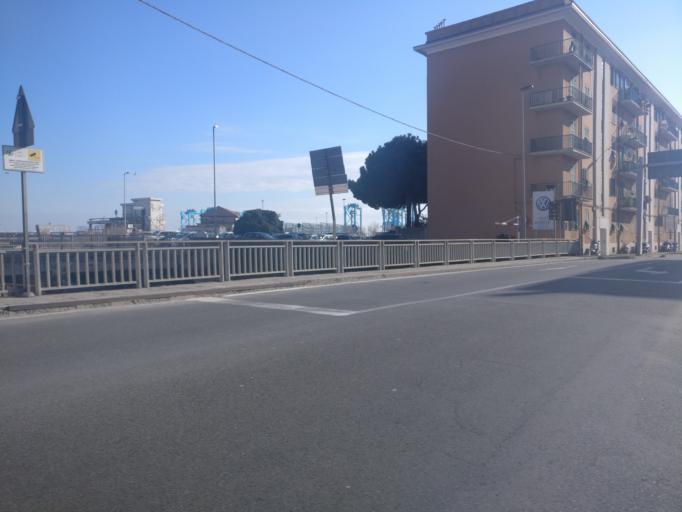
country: IT
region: Liguria
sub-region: Provincia di Savona
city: Vado Ligure
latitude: 44.2702
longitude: 8.4391
